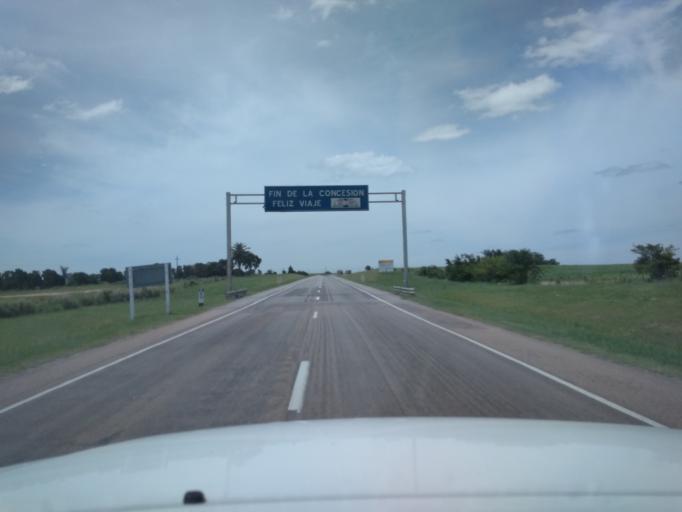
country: UY
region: Florida
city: Cardal
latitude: -34.3221
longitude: -56.2431
